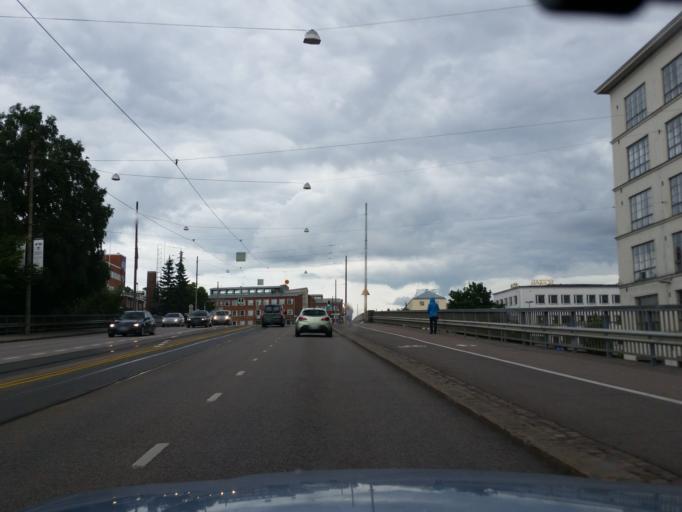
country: FI
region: Uusimaa
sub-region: Helsinki
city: Helsinki
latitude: 60.1915
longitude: 24.9510
